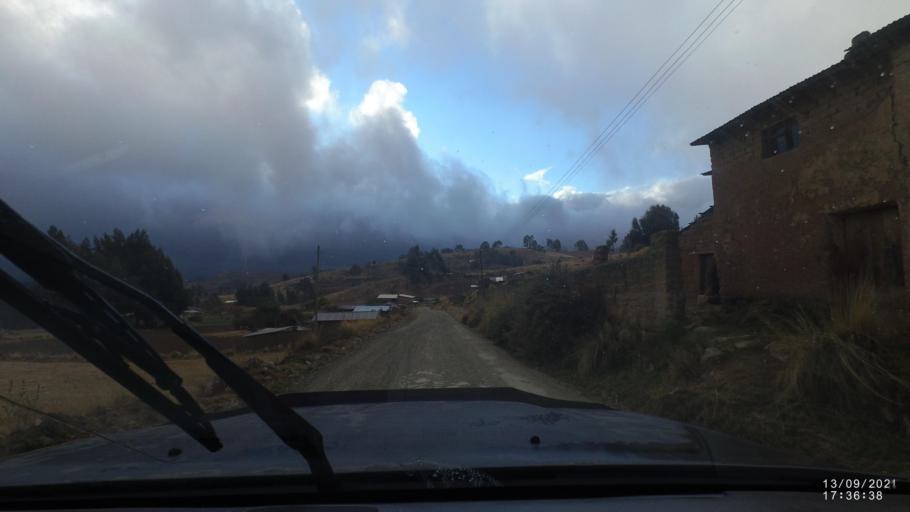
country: BO
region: Cochabamba
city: Colomi
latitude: -17.3625
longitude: -65.8010
